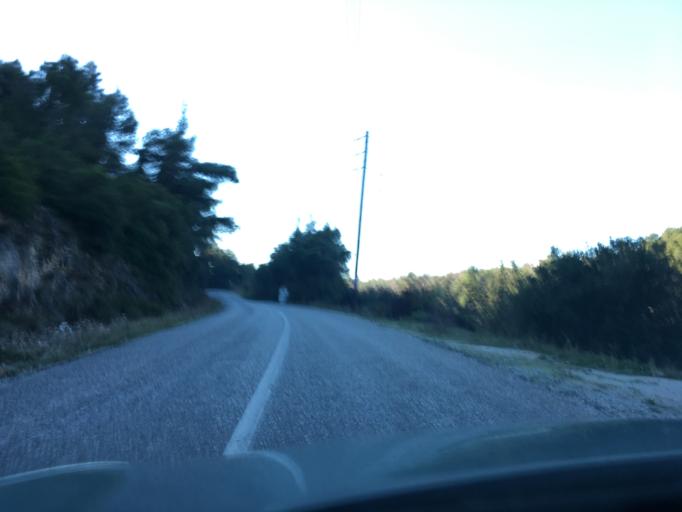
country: GR
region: Thessaly
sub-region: Nomos Magnisias
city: Skopelos
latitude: 39.1025
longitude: 23.7013
